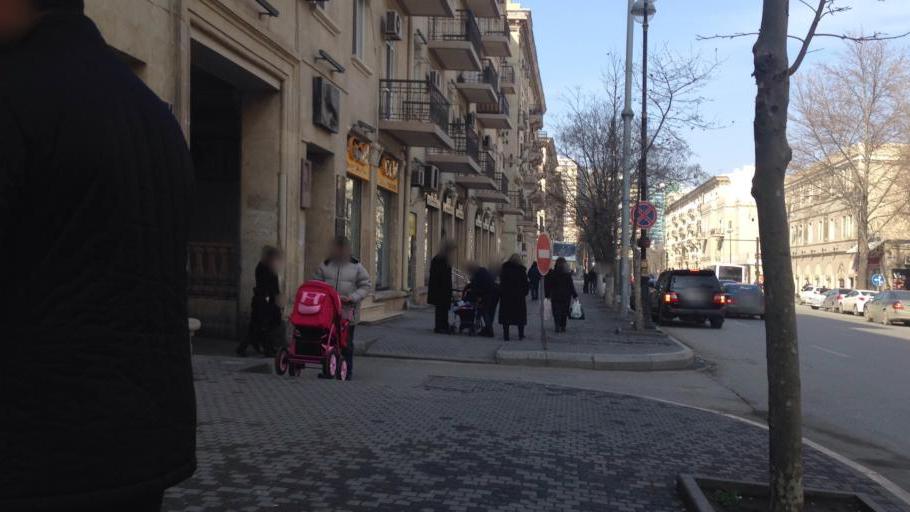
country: AZ
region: Baki
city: Badamdar
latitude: 40.3724
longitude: 49.8334
